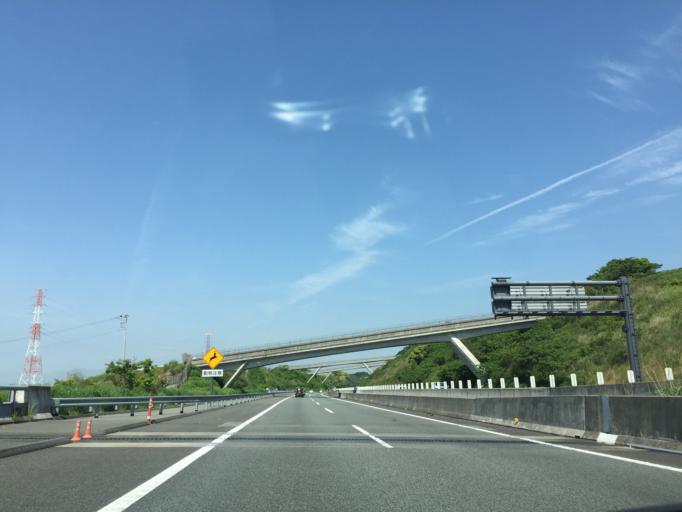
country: JP
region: Shizuoka
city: Fuji
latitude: 35.1600
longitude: 138.7713
